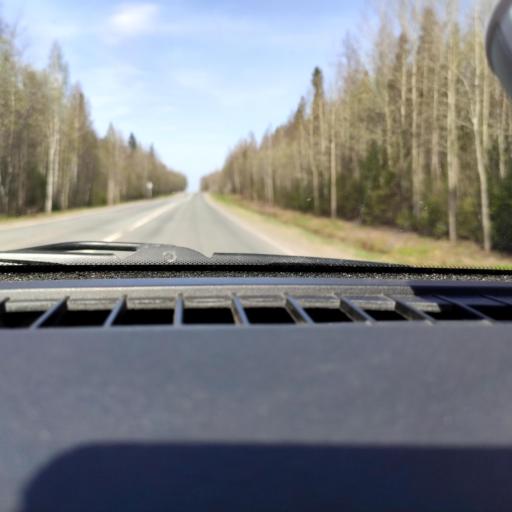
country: RU
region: Perm
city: Perm
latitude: 58.2513
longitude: 56.1607
